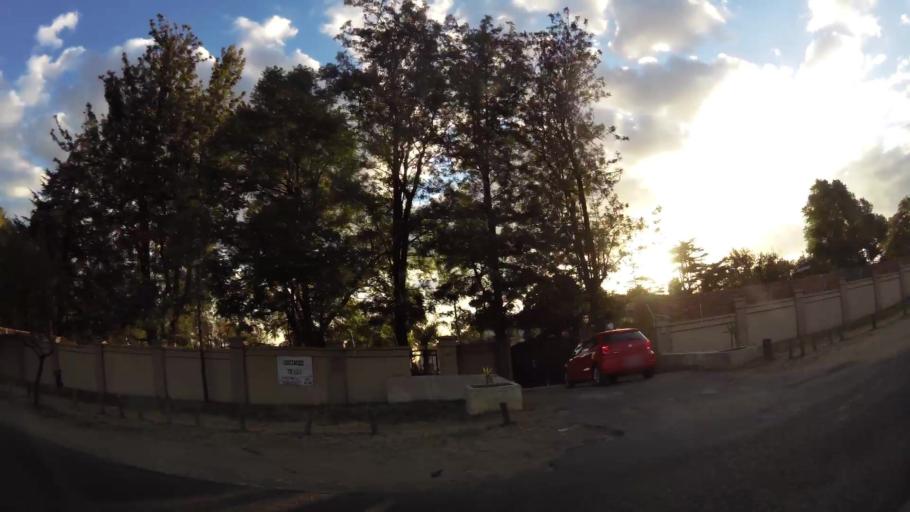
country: ZA
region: Gauteng
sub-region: City of Johannesburg Metropolitan Municipality
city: Midrand
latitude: -25.9604
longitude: 28.1538
